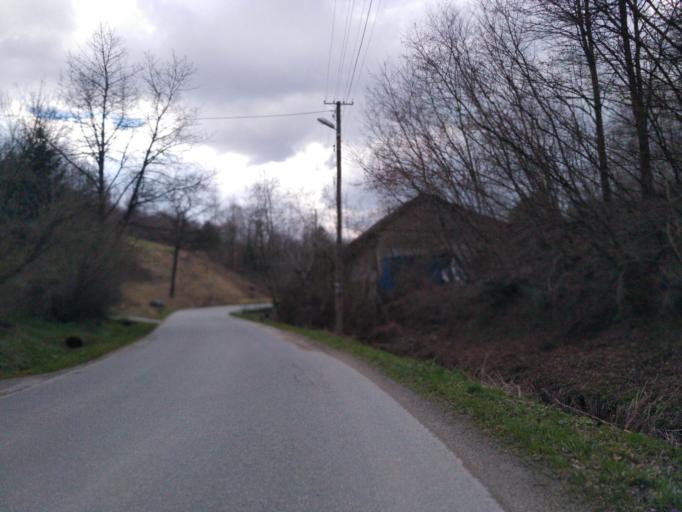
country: PL
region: Subcarpathian Voivodeship
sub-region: Powiat brzozowski
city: Dydnia
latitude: 49.6680
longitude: 22.1910
